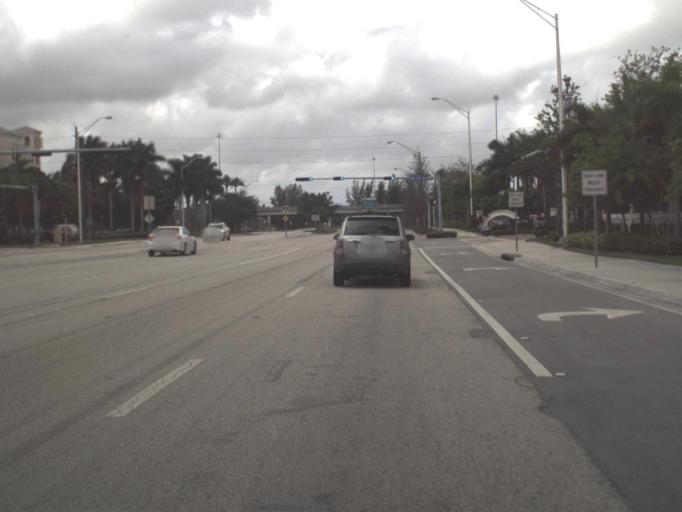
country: US
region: Florida
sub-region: Miami-Dade County
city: Doral
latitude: 25.8118
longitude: -80.3832
